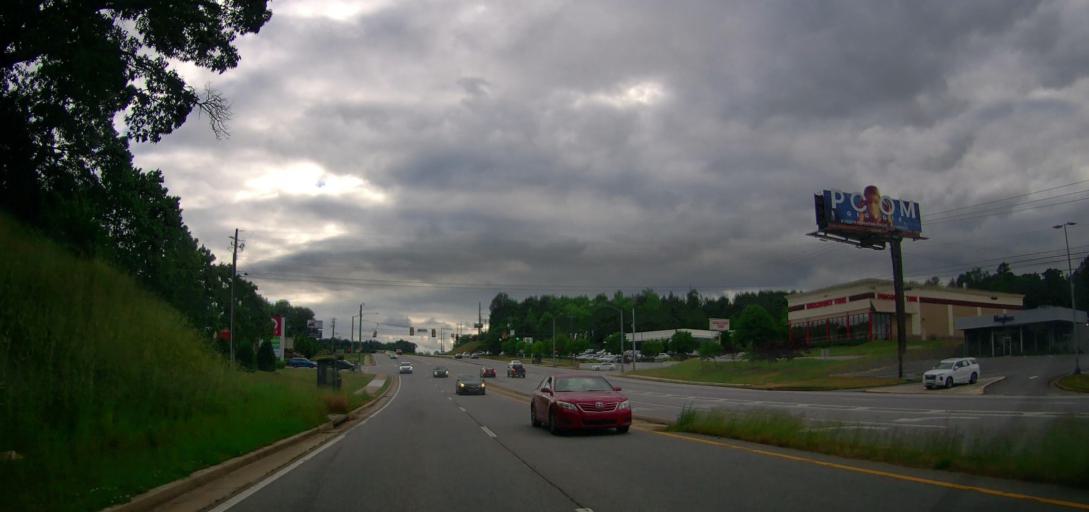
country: US
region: Georgia
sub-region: Clarke County
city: Country Club Estates
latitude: 33.9439
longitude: -83.4399
